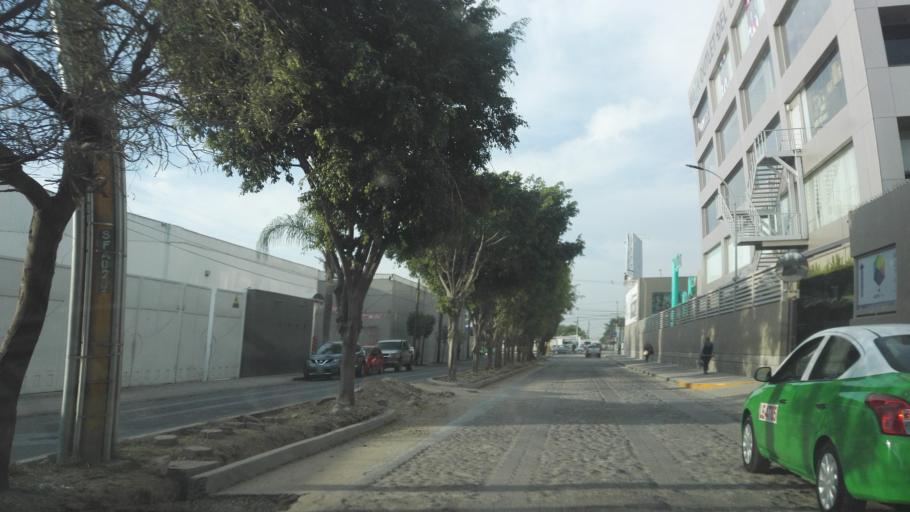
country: MX
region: Guanajuato
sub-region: Leon
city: Fraccionamiento Paraiso Real
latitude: 21.0857
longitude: -101.6130
